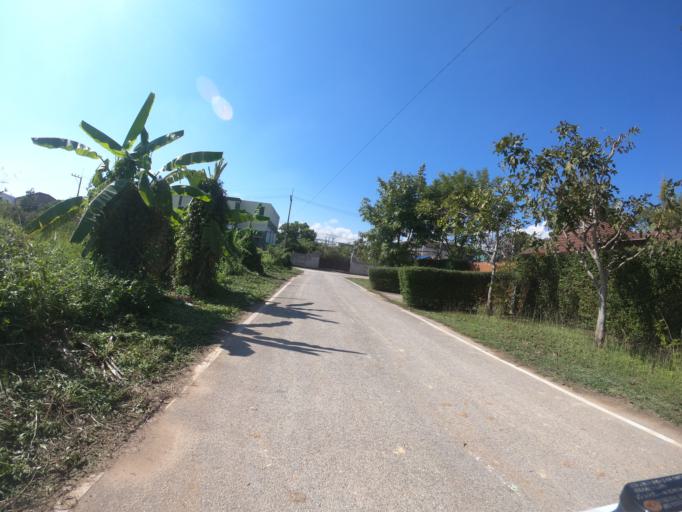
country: TH
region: Chiang Mai
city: Chiang Mai
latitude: 18.7427
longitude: 98.9649
